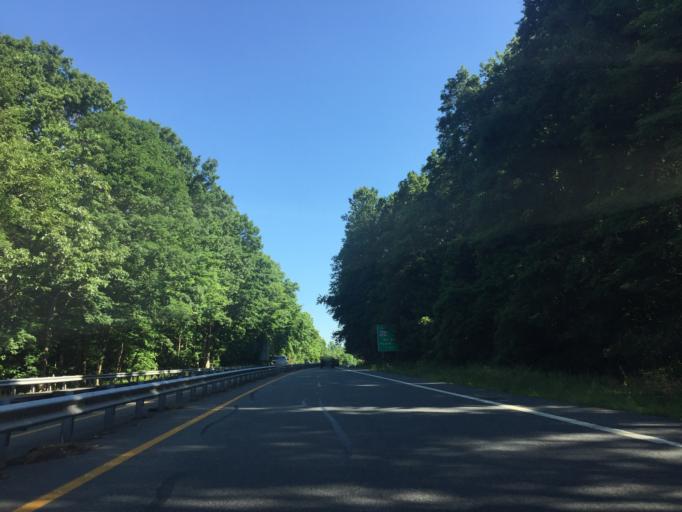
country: US
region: Maryland
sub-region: Harford County
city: North Bel Air
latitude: 39.5358
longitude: -76.3684
